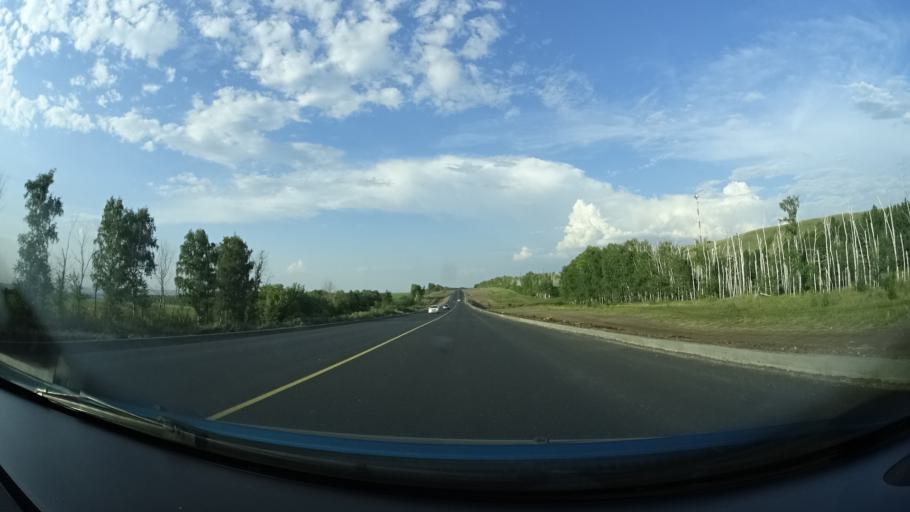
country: RU
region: Samara
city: Sukhodol
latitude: 53.7610
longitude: 50.8816
